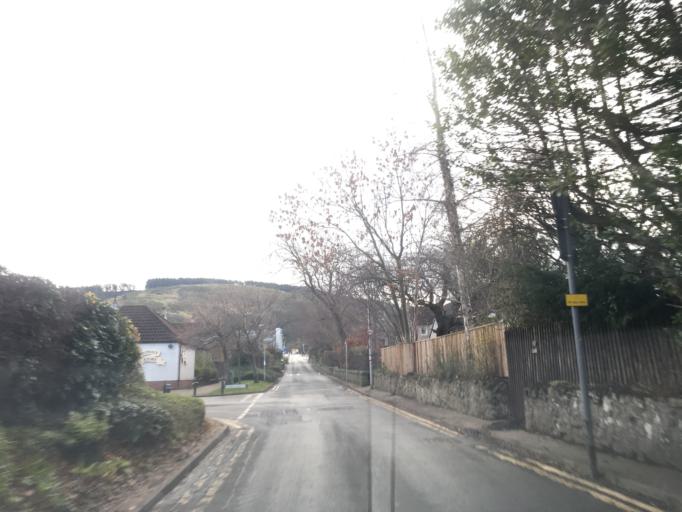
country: GB
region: Scotland
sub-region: Edinburgh
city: Colinton
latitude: 55.9016
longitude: -3.2596
